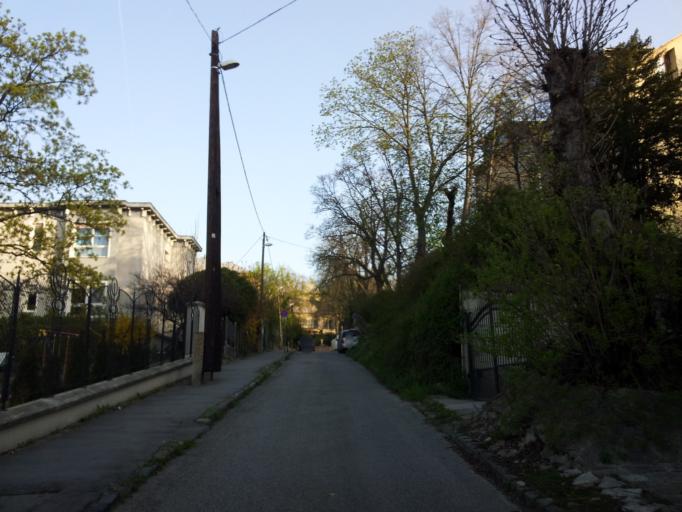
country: HU
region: Budapest
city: Budapest II. keruelet
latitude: 47.5144
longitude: 19.0266
